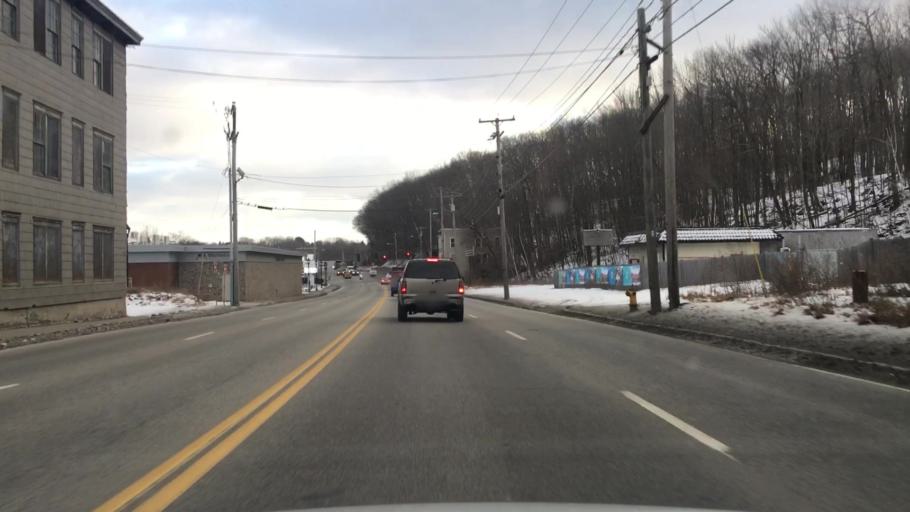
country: US
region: Maine
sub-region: Androscoggin County
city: Auburn
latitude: 44.0957
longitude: -70.2316
